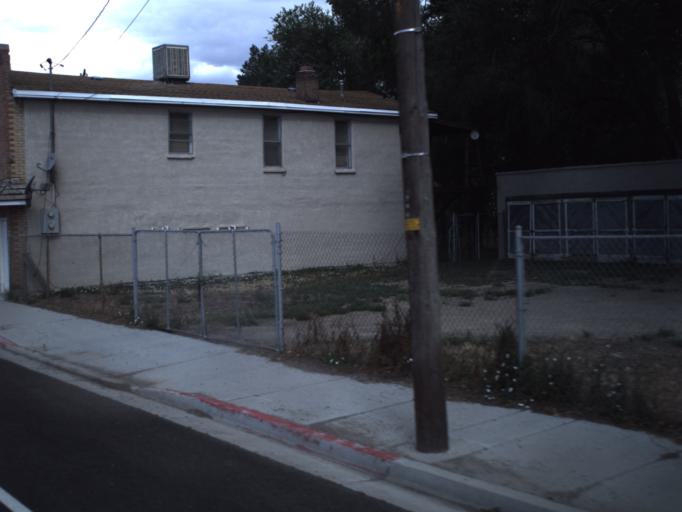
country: US
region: Utah
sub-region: Carbon County
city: Wellington
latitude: 39.5425
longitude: -110.7359
